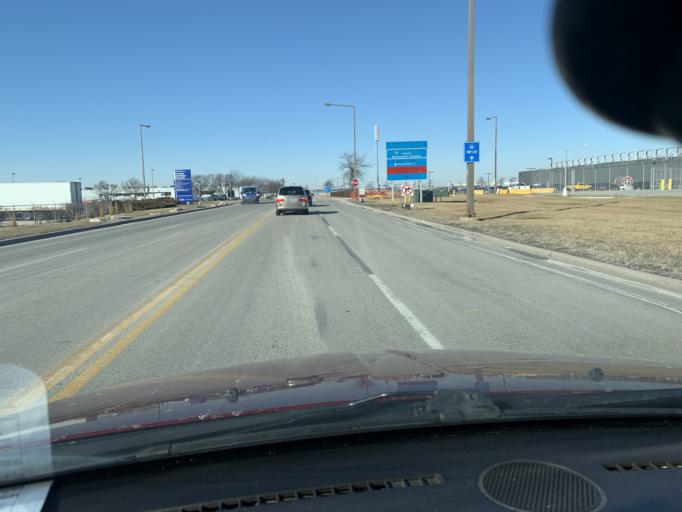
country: US
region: Illinois
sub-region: Cook County
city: Schiller Park
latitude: 41.9622
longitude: -87.8804
